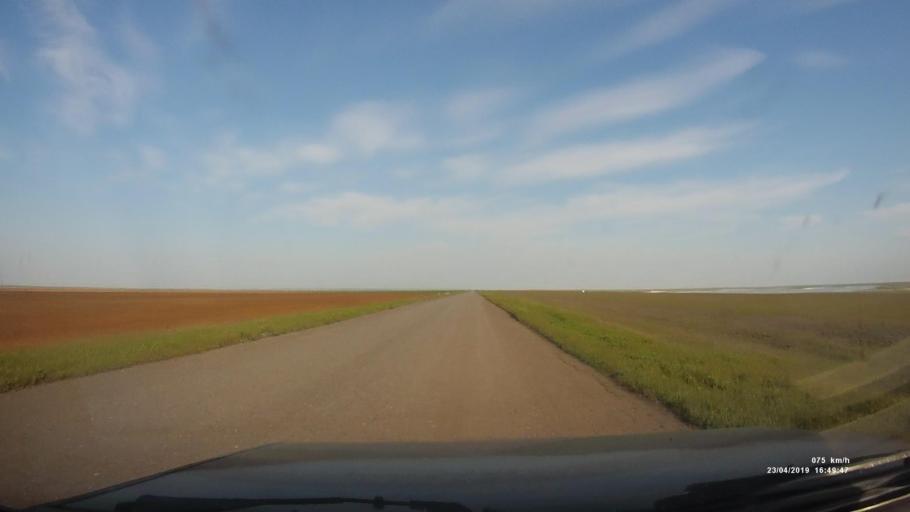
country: RU
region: Kalmykiya
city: Priyutnoye
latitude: 46.3296
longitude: 43.2818
